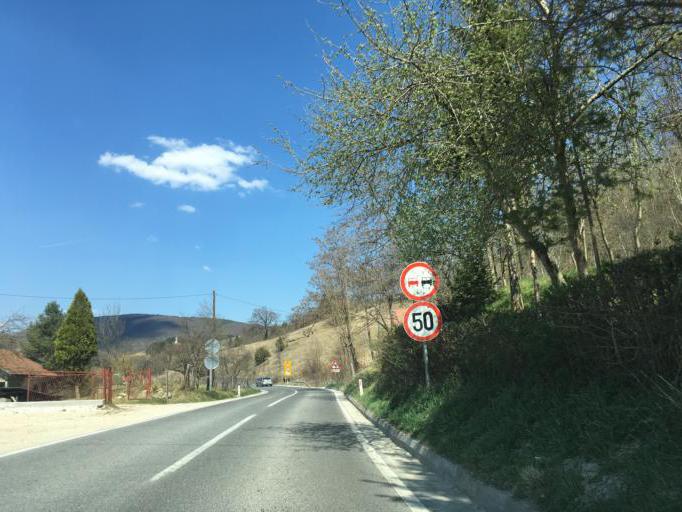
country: BA
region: Federation of Bosnia and Herzegovina
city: Divicani
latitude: 44.3552
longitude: 17.3000
